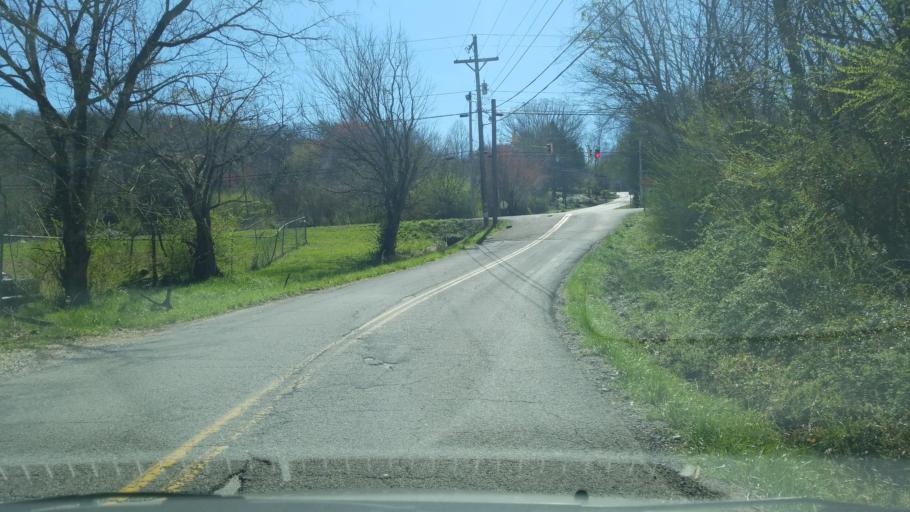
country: US
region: Tennessee
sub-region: Hamilton County
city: Falling Water
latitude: 35.1706
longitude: -85.2573
